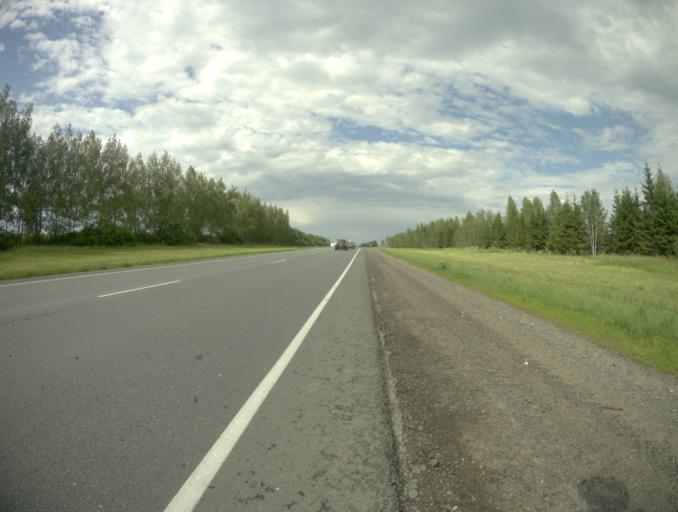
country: RU
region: Vladimir
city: Suzdal'
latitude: 56.3380
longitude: 40.4742
